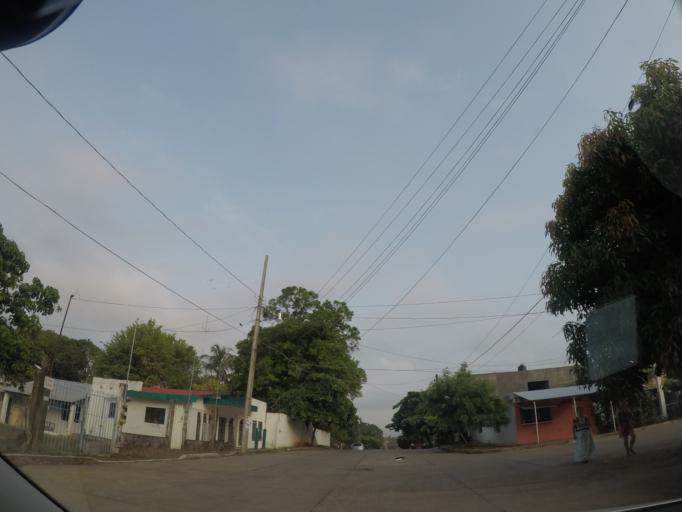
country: MX
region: Oaxaca
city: Matias Romero
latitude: 16.8710
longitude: -95.0411
